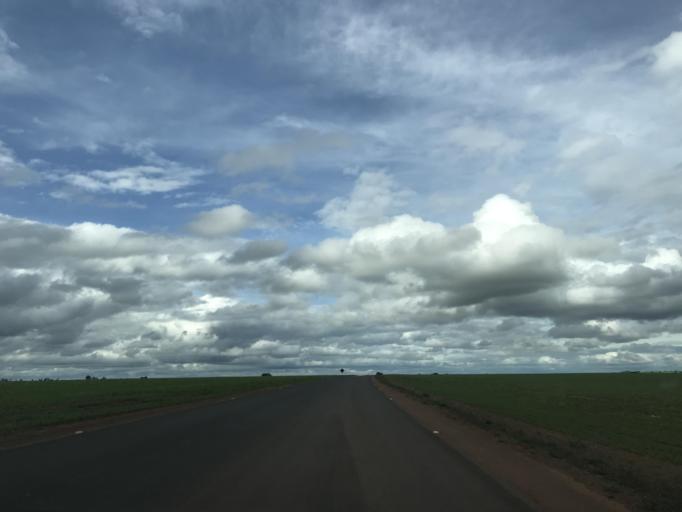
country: BR
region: Goias
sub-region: Vianopolis
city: Vianopolis
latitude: -16.9725
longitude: -48.6580
